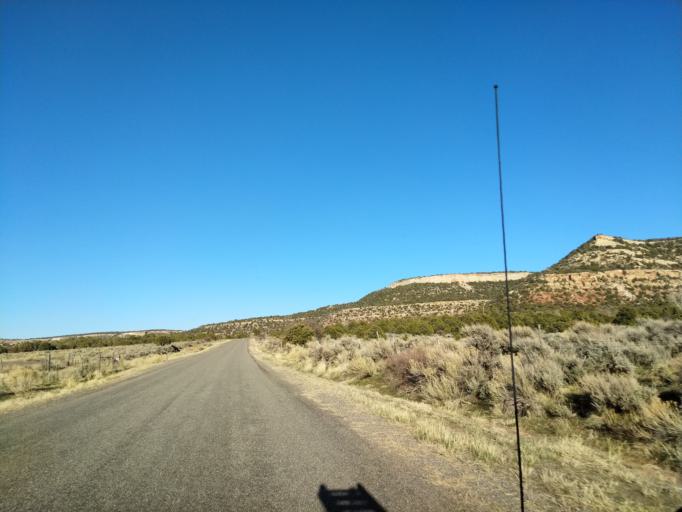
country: US
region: Colorado
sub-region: Mesa County
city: Loma
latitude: 38.9548
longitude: -109.0280
